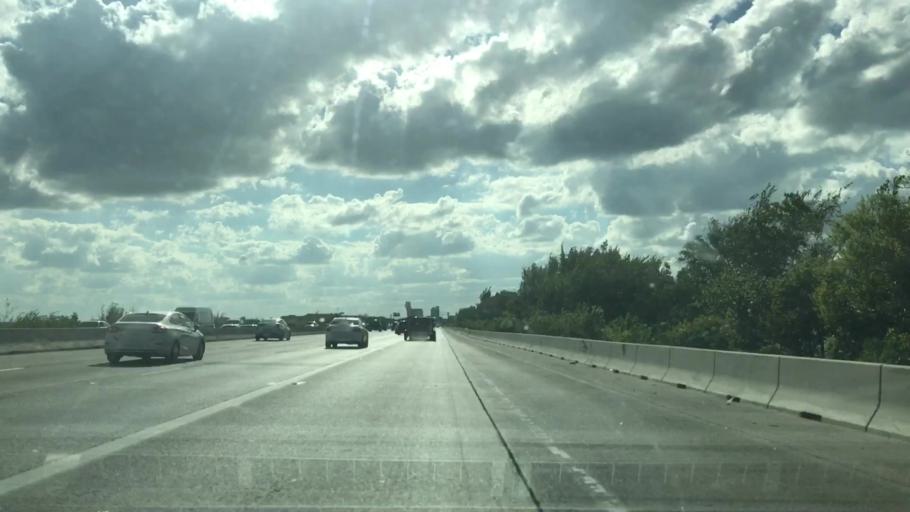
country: US
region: Texas
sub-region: Dallas County
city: Rowlett
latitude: 32.8734
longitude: -96.5252
